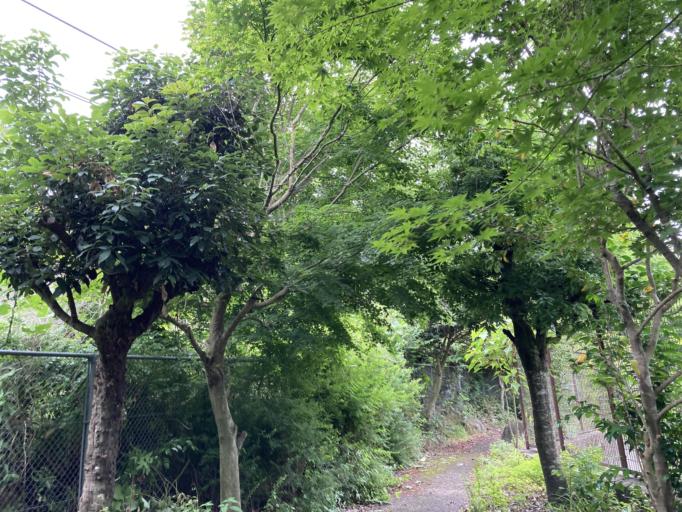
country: JP
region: Nara
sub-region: Ikoma-shi
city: Ikoma
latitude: 34.6455
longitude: 135.7069
